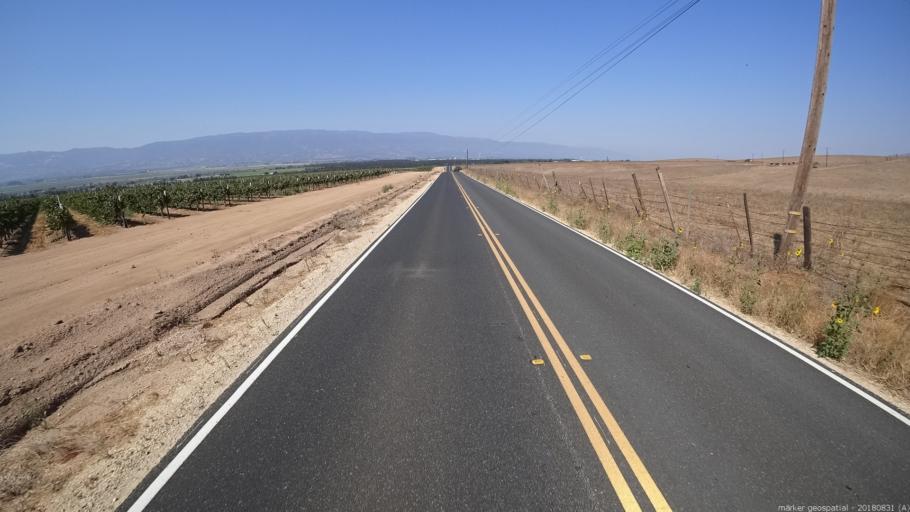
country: US
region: California
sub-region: Monterey County
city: Soledad
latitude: 36.4159
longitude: -121.2693
